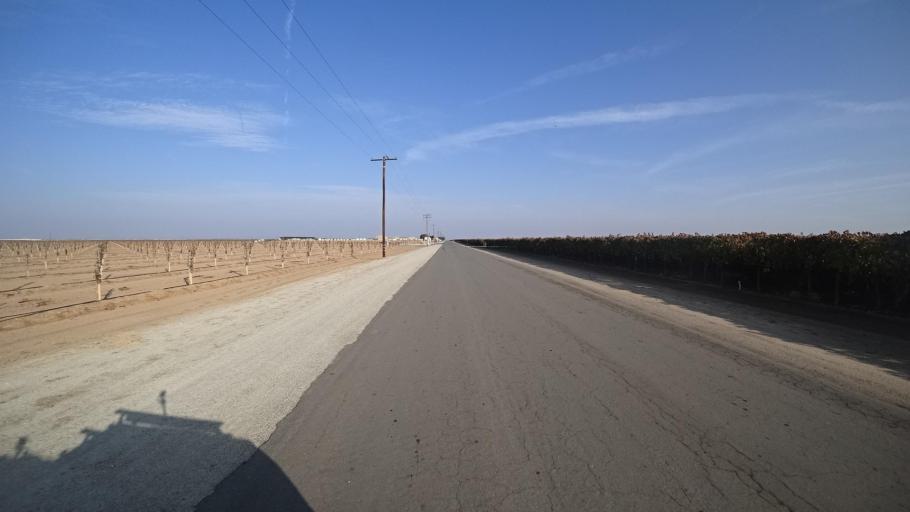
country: US
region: California
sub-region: Kern County
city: McFarland
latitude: 35.6936
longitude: -119.1870
